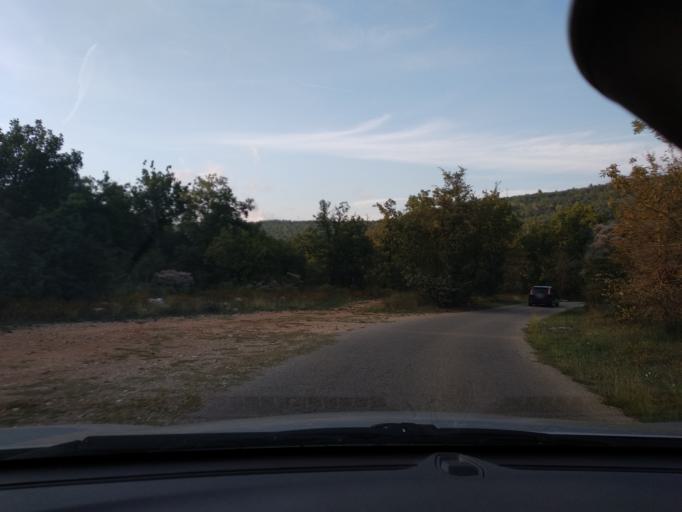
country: FR
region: Provence-Alpes-Cote d'Azur
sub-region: Departement des Alpes-Maritimes
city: Saint-Cezaire-sur-Siagne
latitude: 43.6550
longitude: 6.8102
